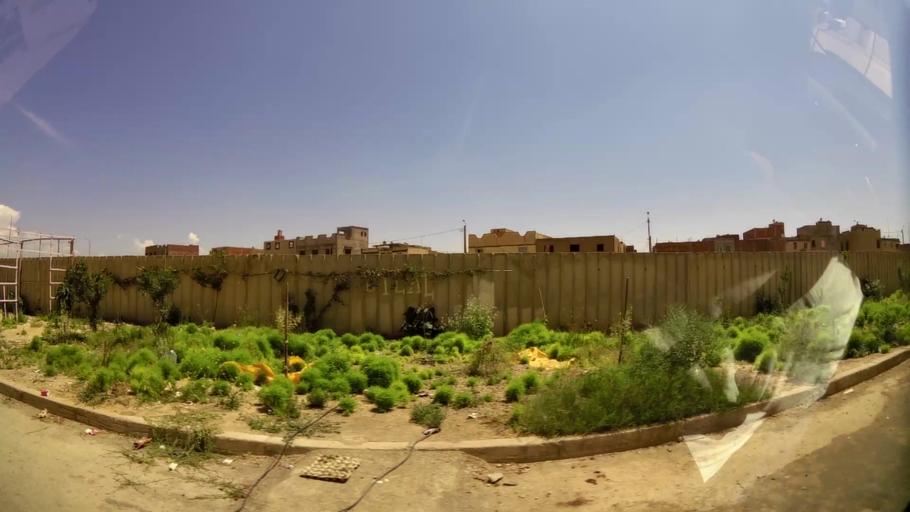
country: MA
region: Oriental
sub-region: Oujda-Angad
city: Oujda
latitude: 34.6944
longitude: -1.9402
